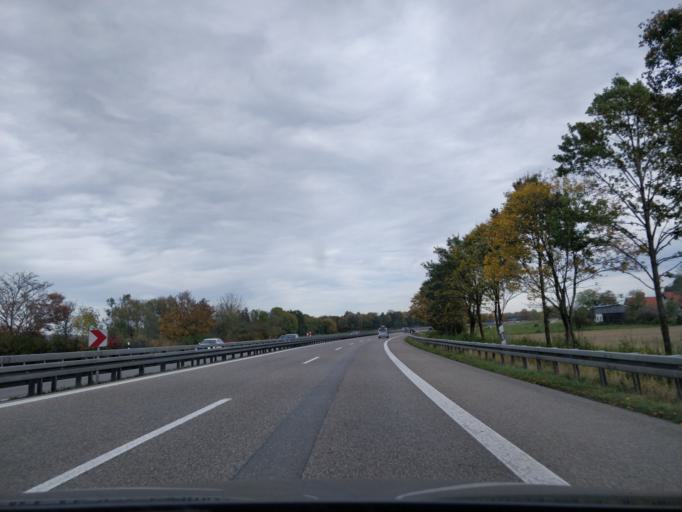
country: DE
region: Bavaria
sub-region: Swabia
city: Waal
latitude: 48.0453
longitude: 10.8108
